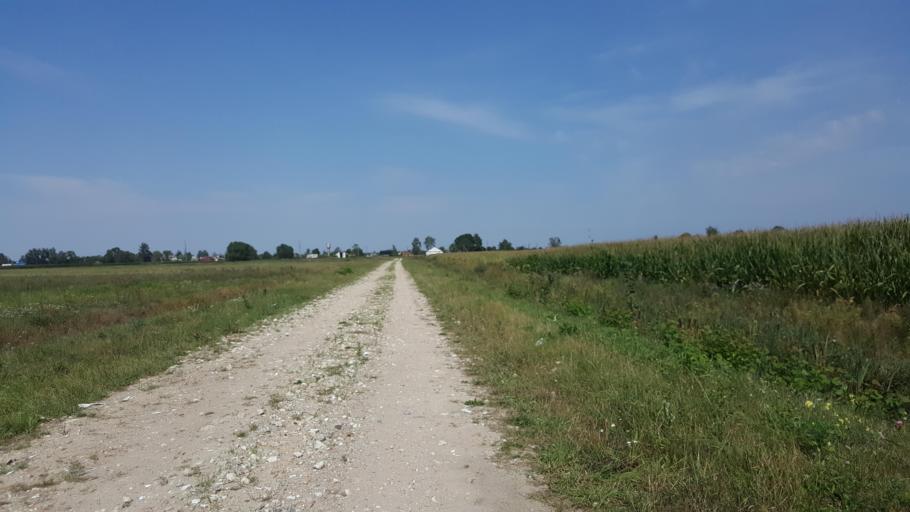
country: PL
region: Podlasie
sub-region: Powiat hajnowski
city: Czeremcha
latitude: 52.4883
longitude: 23.5726
